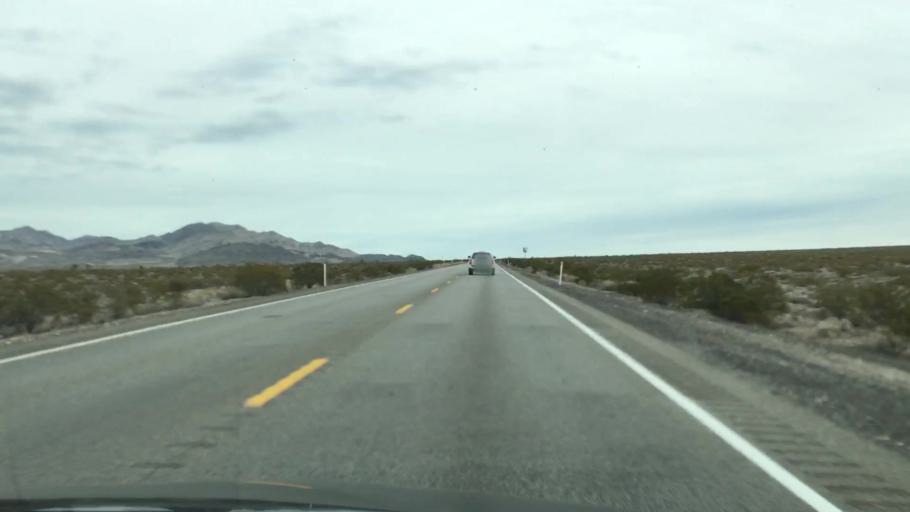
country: US
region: Nevada
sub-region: Nye County
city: Pahrump
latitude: 36.5919
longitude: -116.0319
